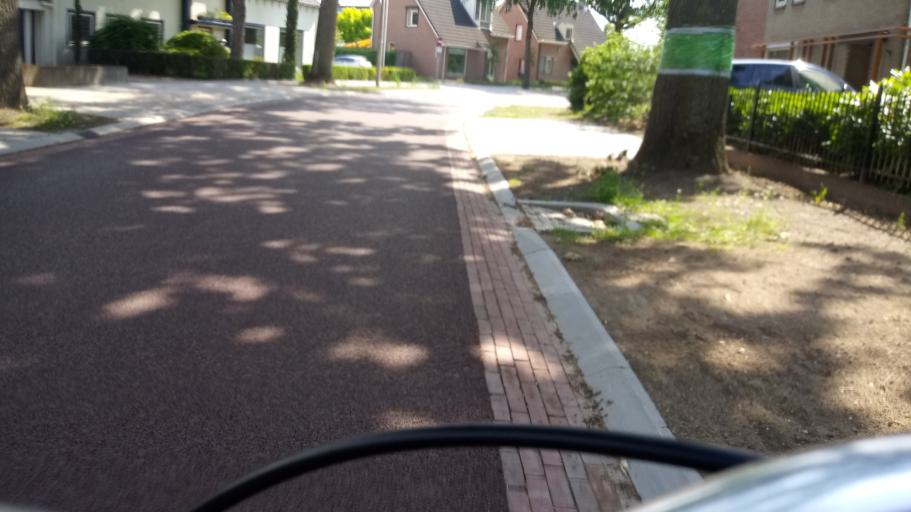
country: NL
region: Gelderland
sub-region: Gemeente Nijmegen
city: Nijmegen
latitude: 51.8401
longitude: 5.8285
